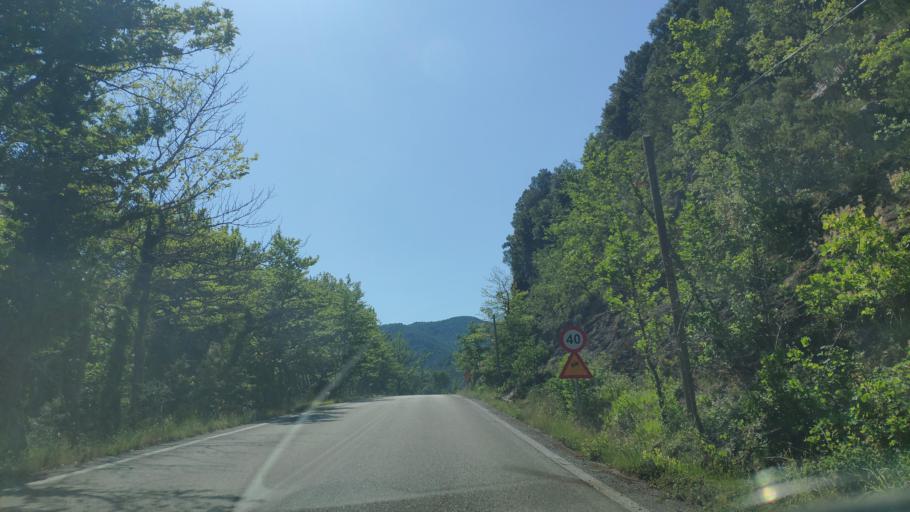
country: GR
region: West Greece
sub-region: Nomos Aitolias kai Akarnanias
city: Sardinia
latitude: 38.9245
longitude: 21.3560
